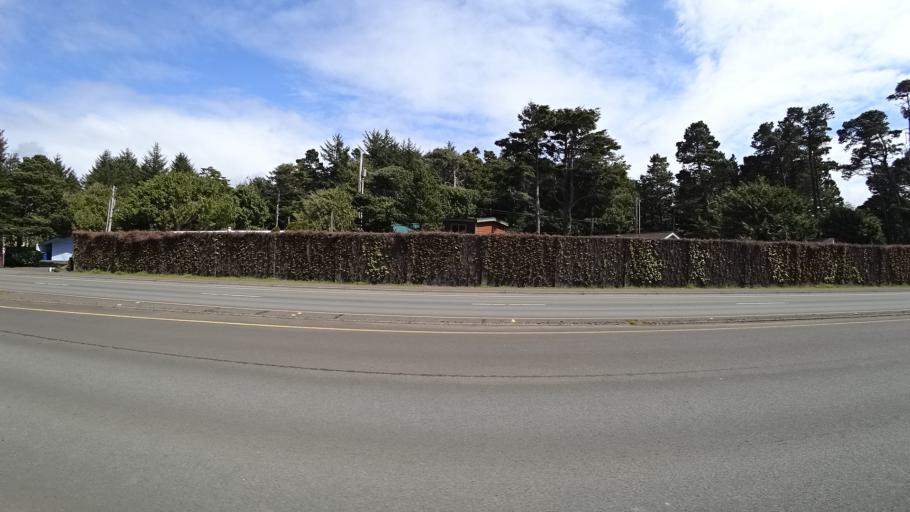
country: US
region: Oregon
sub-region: Lincoln County
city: Lincoln Beach
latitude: 44.8469
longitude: -124.0460
